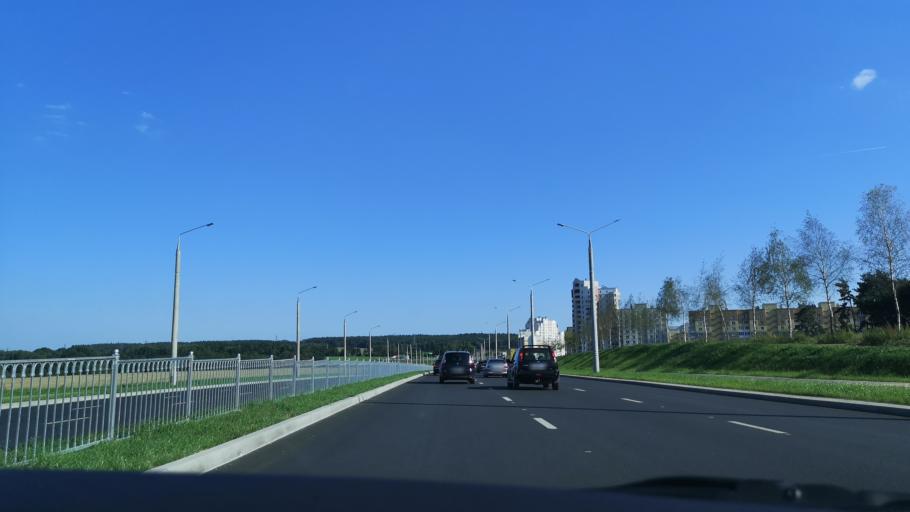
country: BY
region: Grodnenskaya
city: Hrodna
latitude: 53.6491
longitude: 23.8621
